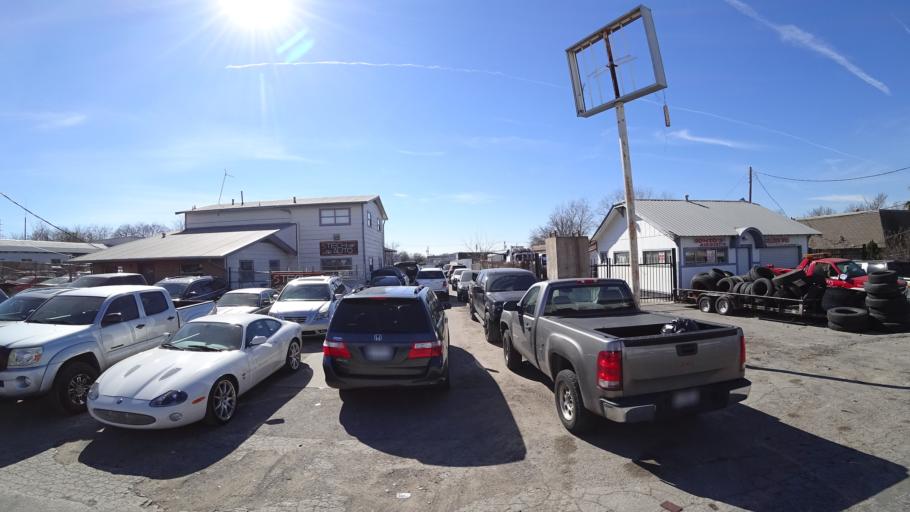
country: US
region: Texas
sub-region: Travis County
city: Wells Branch
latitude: 30.3795
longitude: -97.6903
